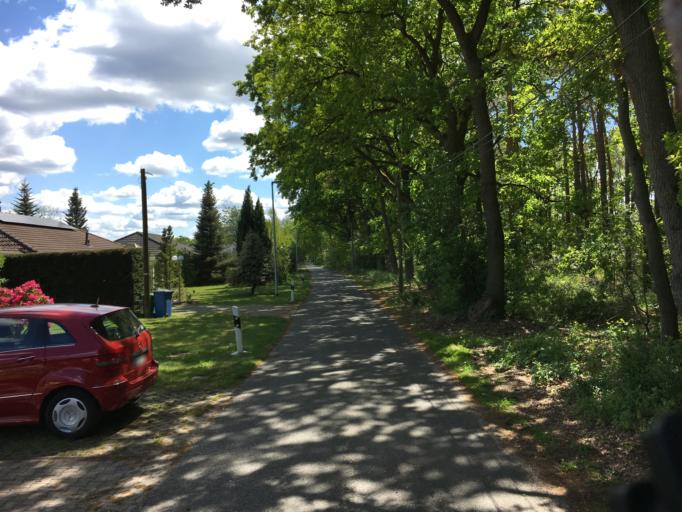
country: DE
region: Brandenburg
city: Trebbin
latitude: 52.1812
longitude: 13.2136
